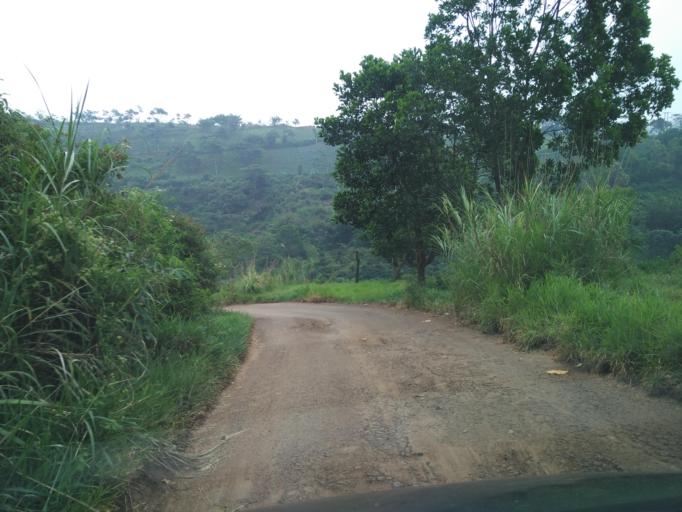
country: ID
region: West Java
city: Caringin
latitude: -6.6741
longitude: 107.0189
